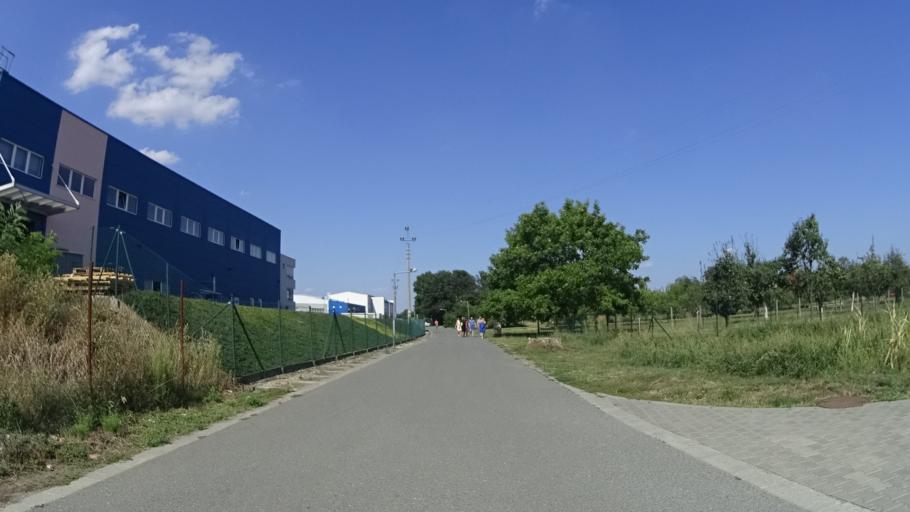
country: CZ
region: Zlin
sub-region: Okres Zlin
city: Ostrozska Nova Ves
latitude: 49.0023
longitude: 17.4288
